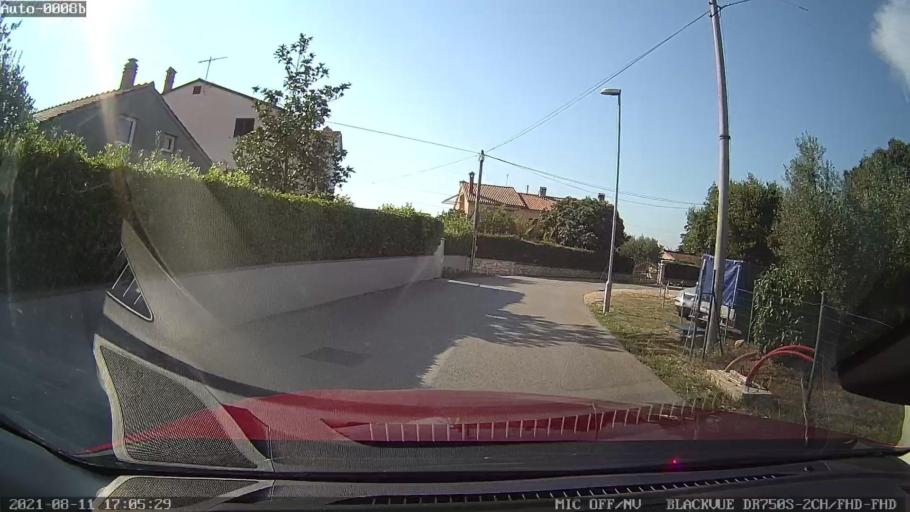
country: HR
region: Istarska
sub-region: Grad Rovinj
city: Rovinj
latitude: 45.0823
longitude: 13.6646
